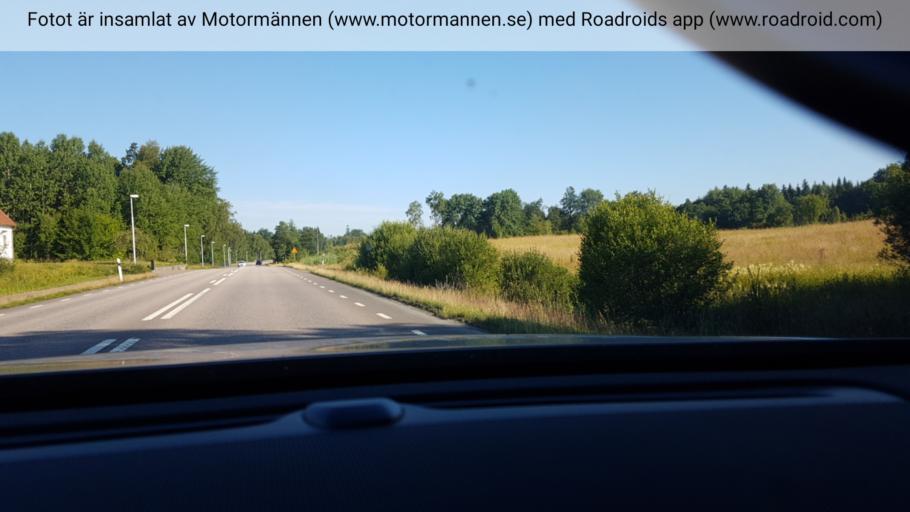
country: SE
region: Skane
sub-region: Hassleholms Kommun
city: Bjarnum
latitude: 56.3119
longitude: 13.6917
